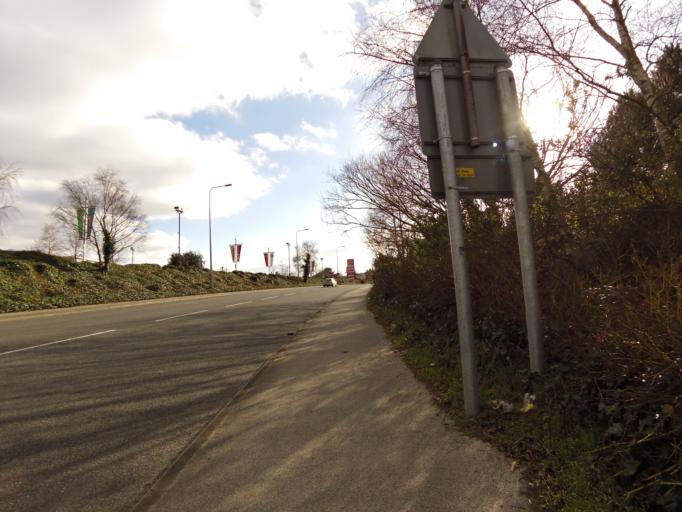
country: GB
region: England
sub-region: Suffolk
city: Kesgrave
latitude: 52.0345
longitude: 1.2068
